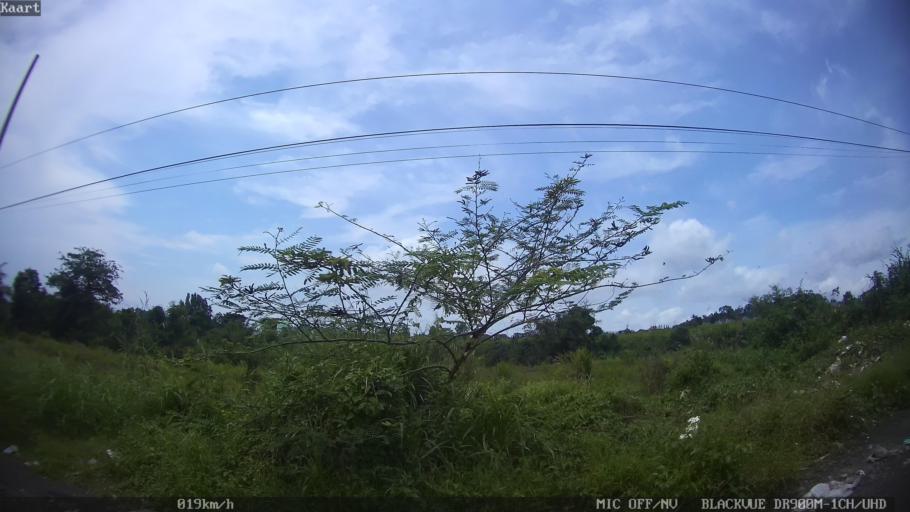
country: ID
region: Lampung
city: Bandarlampung
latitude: -5.4064
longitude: 105.1995
